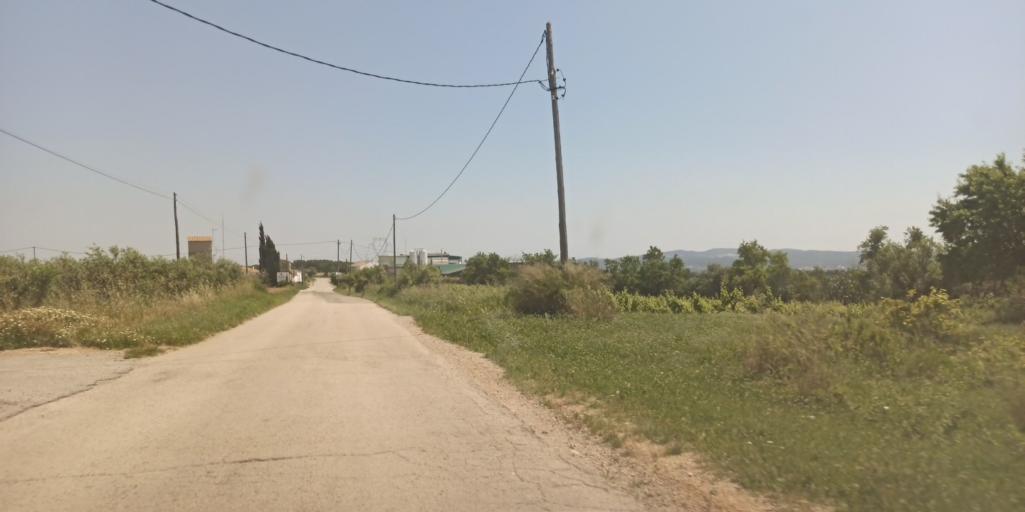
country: ES
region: Catalonia
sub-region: Provincia de Barcelona
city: Sant Marti Sarroca
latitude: 41.3812
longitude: 1.6265
